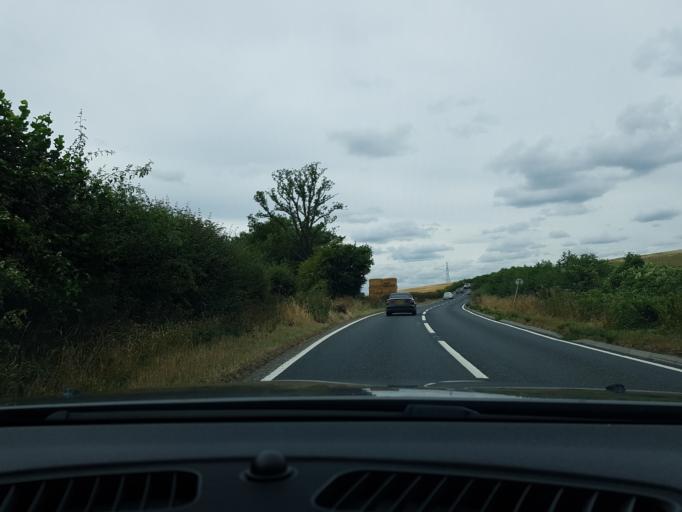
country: GB
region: England
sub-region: Hampshire
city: Kingsclere
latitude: 51.3061
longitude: -1.1944
